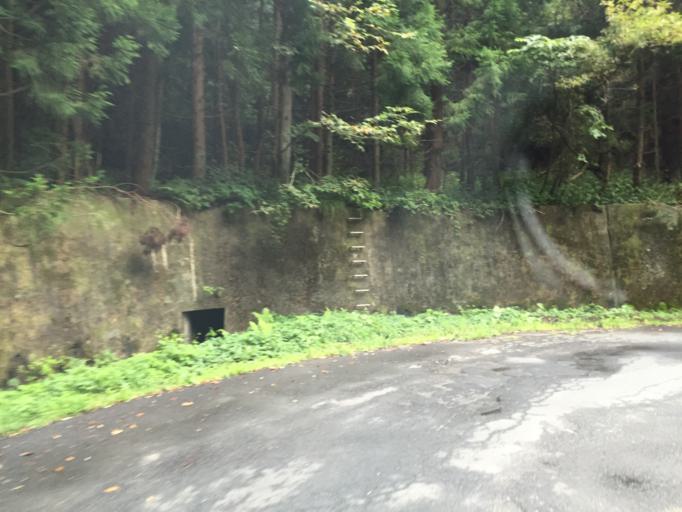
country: JP
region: Fukushima
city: Fukushima-shi
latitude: 37.7992
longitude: 140.3741
